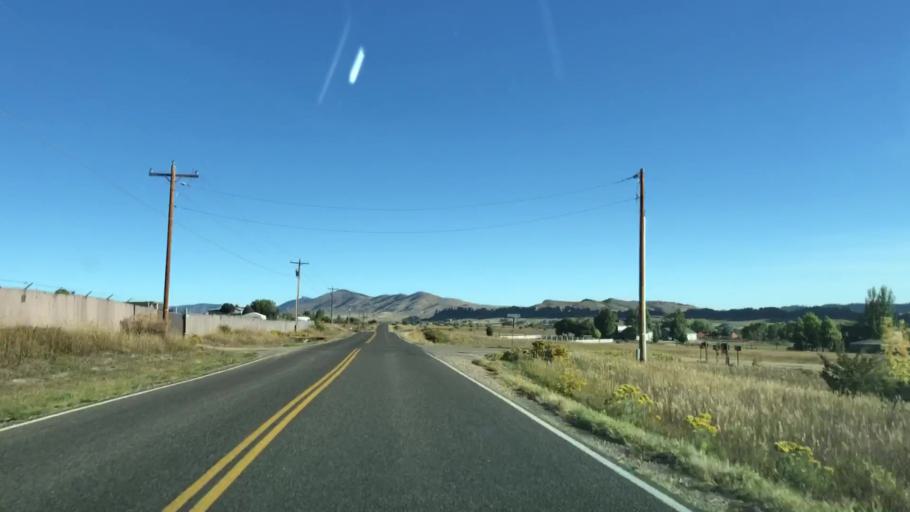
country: US
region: Colorado
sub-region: Larimer County
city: Loveland
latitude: 40.3954
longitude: -105.1682
